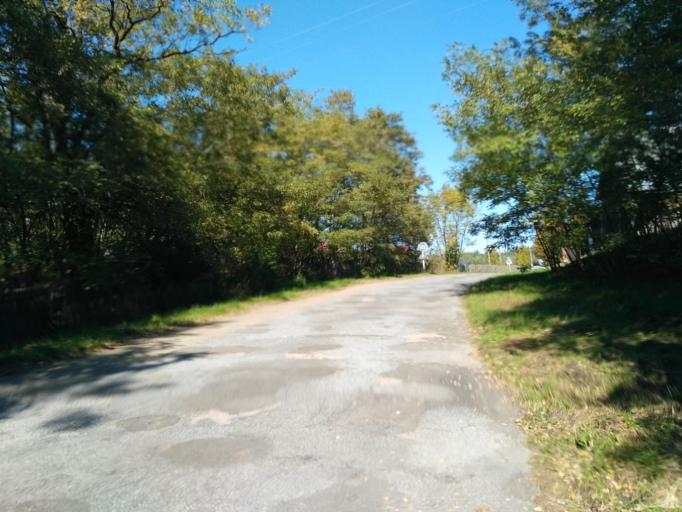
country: PL
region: Subcarpathian Voivodeship
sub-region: Powiat debicki
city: Debica
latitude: 49.9723
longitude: 21.3836
